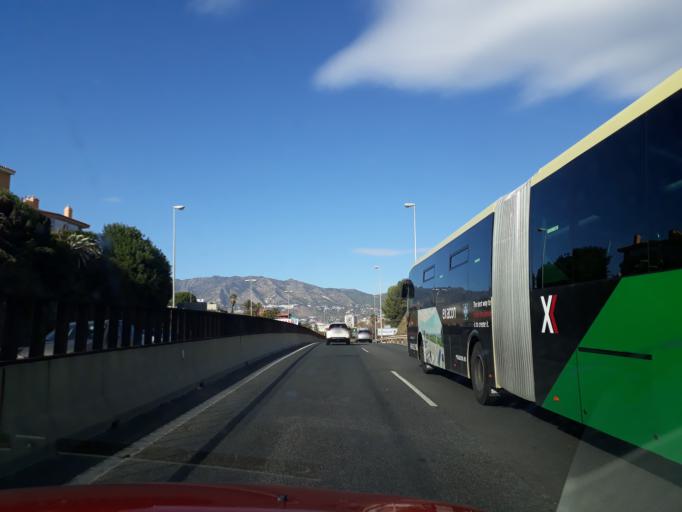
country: ES
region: Andalusia
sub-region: Provincia de Malaga
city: Fuengirola
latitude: 36.5241
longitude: -4.6302
